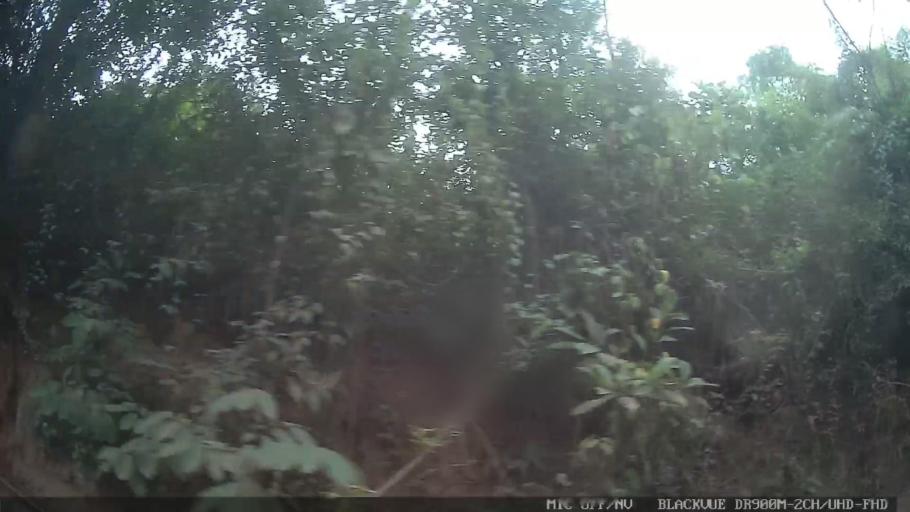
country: BR
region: Sao Paulo
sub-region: Bom Jesus Dos Perdoes
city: Bom Jesus dos Perdoes
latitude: -23.1407
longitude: -46.5059
